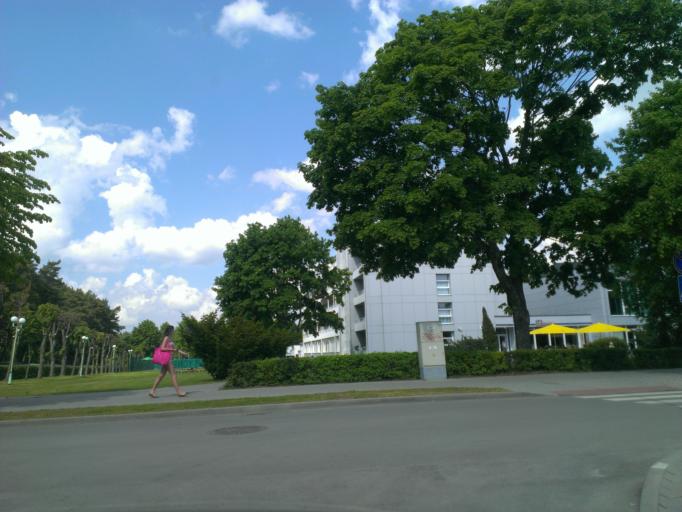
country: LT
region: Klaipedos apskritis
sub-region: Klaipeda
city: Palanga
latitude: 55.9267
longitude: 21.0632
